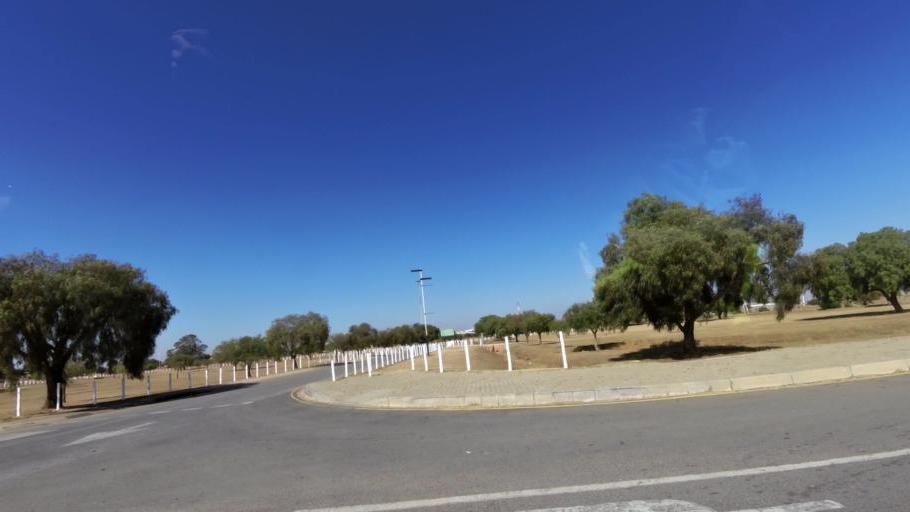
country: ZA
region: Gauteng
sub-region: City of Johannesburg Metropolitan Municipality
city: Johannesburg
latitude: -26.2455
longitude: 27.9764
